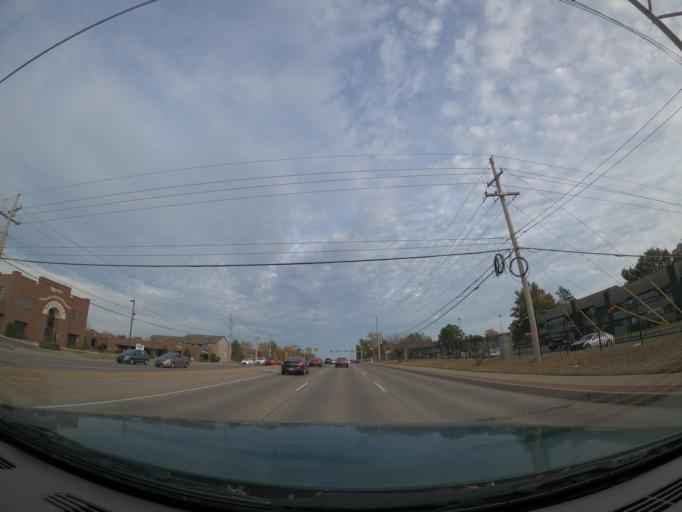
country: US
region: Oklahoma
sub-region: Tulsa County
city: Jenks
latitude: 36.0608
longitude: -95.9131
